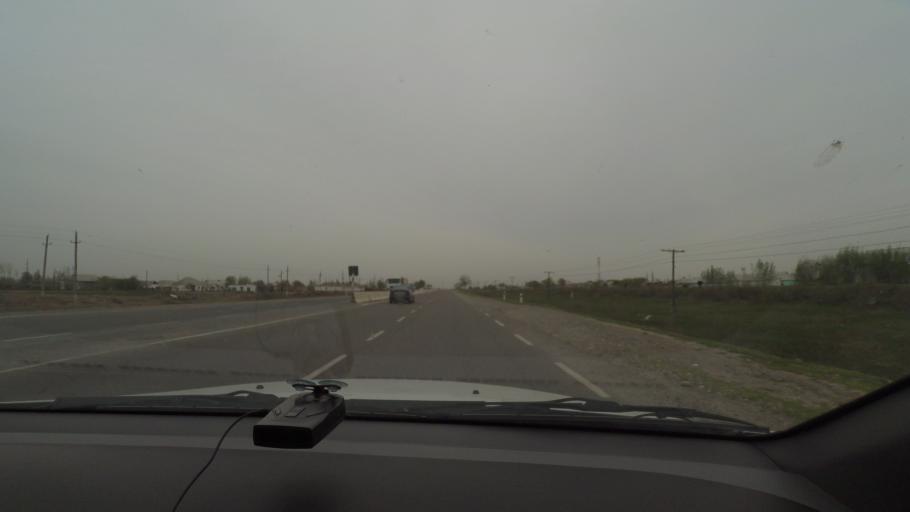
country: UZ
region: Sirdaryo
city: Guliston
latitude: 40.4950
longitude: 68.6430
